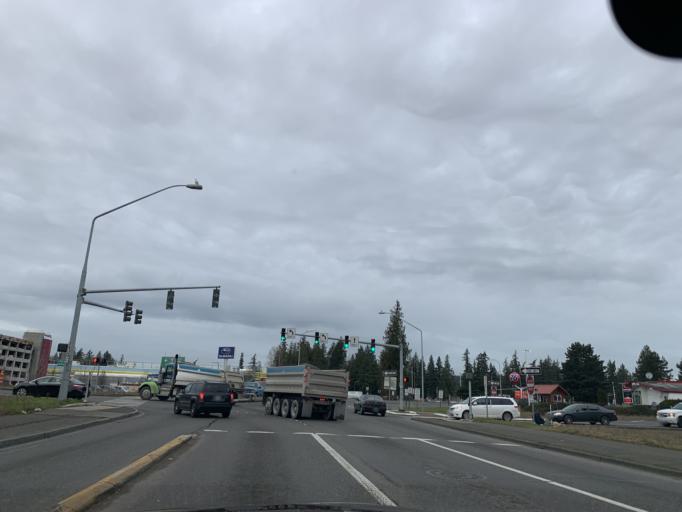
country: US
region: Washington
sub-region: Snohomish County
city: Marysville
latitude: 48.0519
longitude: -122.1850
